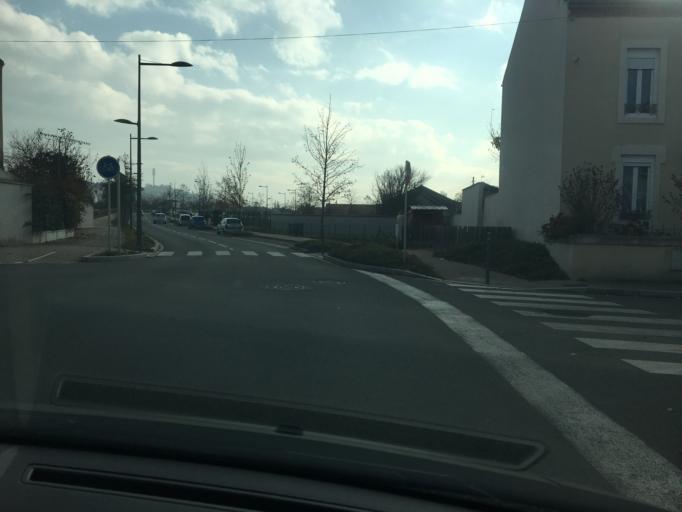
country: FR
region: Auvergne
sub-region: Departement de l'Allier
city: Vichy
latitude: 46.1261
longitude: 3.4366
